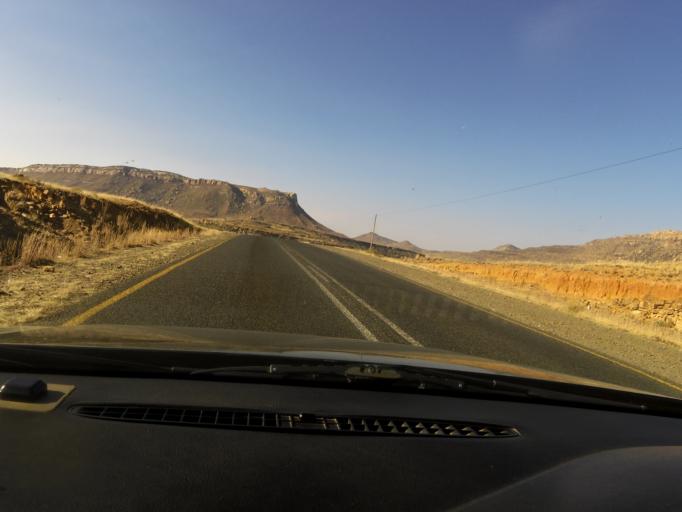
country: LS
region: Mafeteng
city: Mafeteng
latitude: -29.8992
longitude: 27.2528
